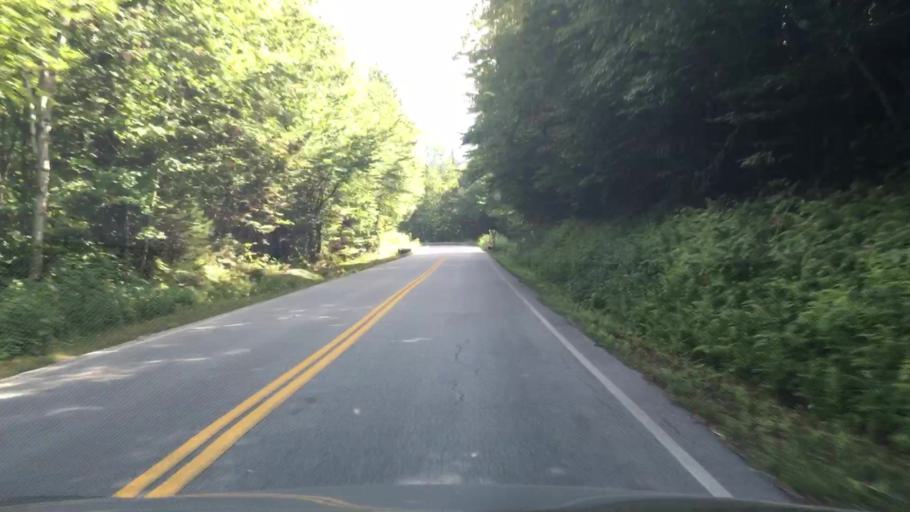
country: US
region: New Hampshire
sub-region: Carroll County
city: Tamworth
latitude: 44.0239
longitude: -71.3212
